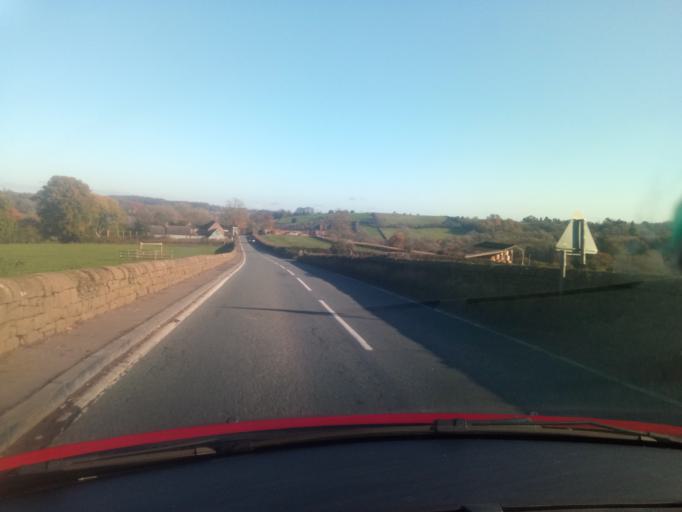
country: GB
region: England
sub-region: Derbyshire
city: Belper
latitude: 53.0225
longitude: -1.5208
